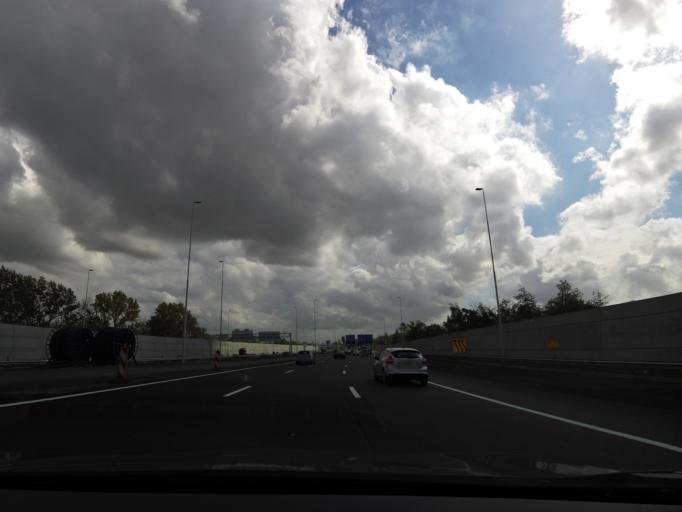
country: NL
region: South Holland
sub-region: Gemeente Schiedam
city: Schiedam
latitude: 51.9220
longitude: 4.3657
